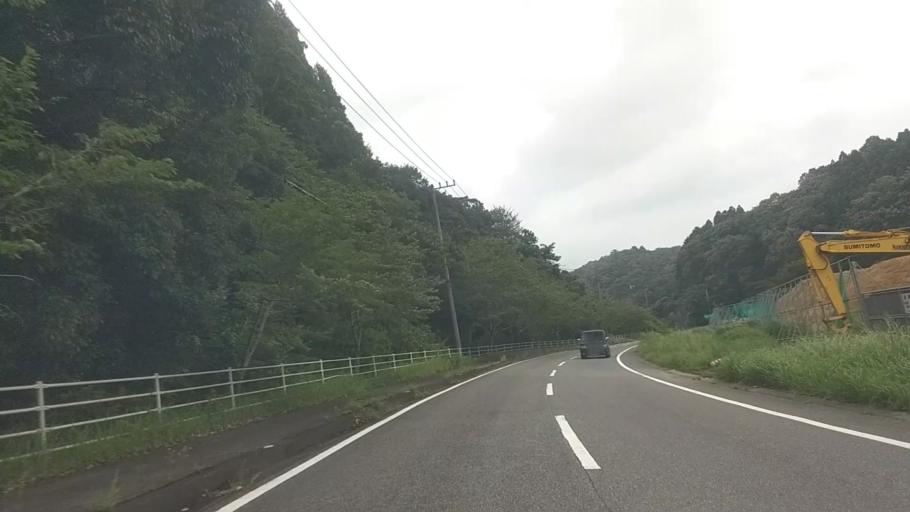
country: JP
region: Chiba
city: Kawaguchi
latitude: 35.2469
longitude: 140.0381
